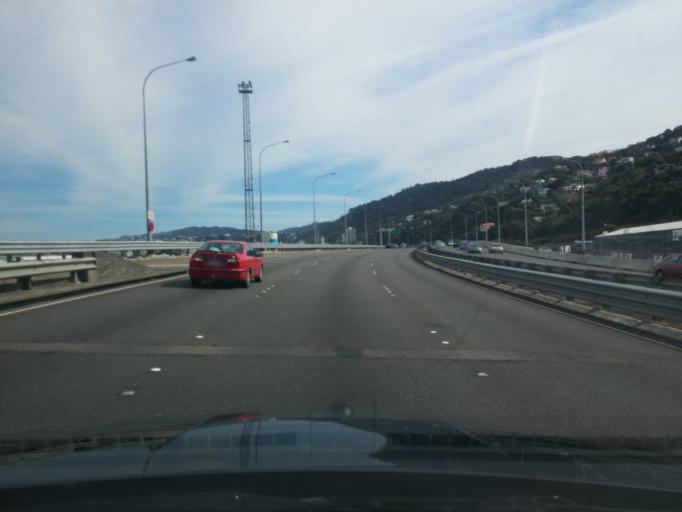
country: NZ
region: Wellington
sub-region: Wellington City
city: Wellington
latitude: -41.2613
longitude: 174.7909
